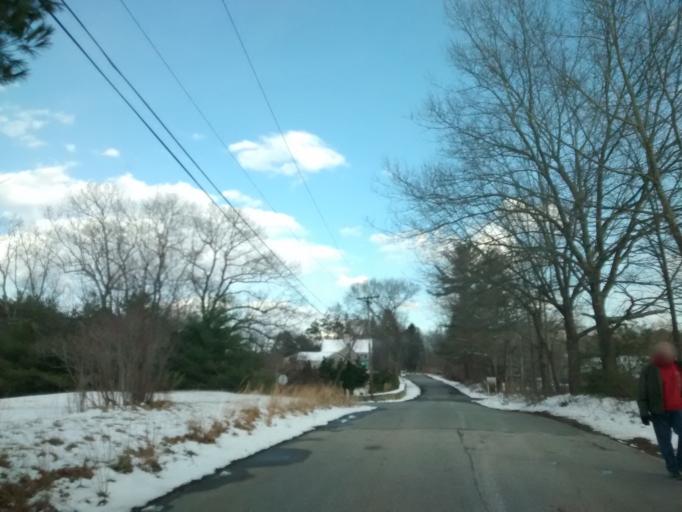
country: US
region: Massachusetts
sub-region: Worcester County
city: East Douglas
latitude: 42.0306
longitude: -71.6748
